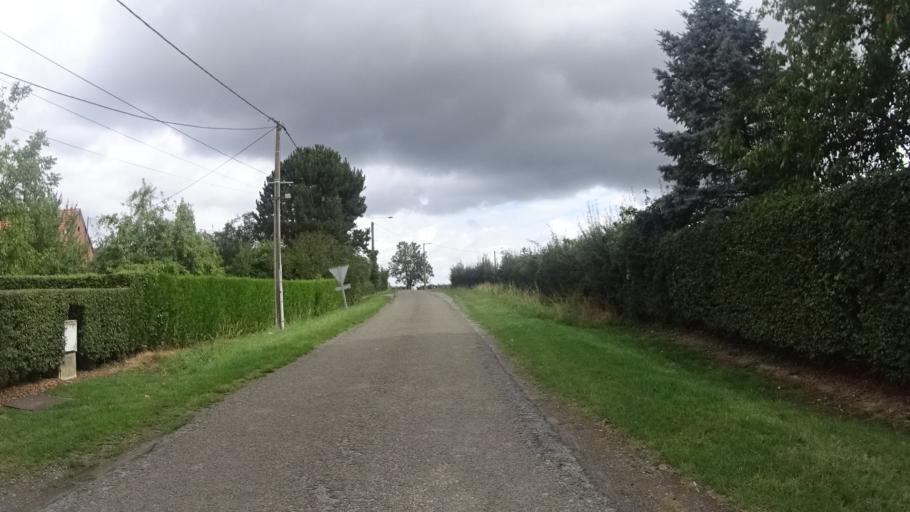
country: FR
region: Nord-Pas-de-Calais
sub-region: Departement du Nord
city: Landrecies
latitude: 50.1197
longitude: 3.7069
